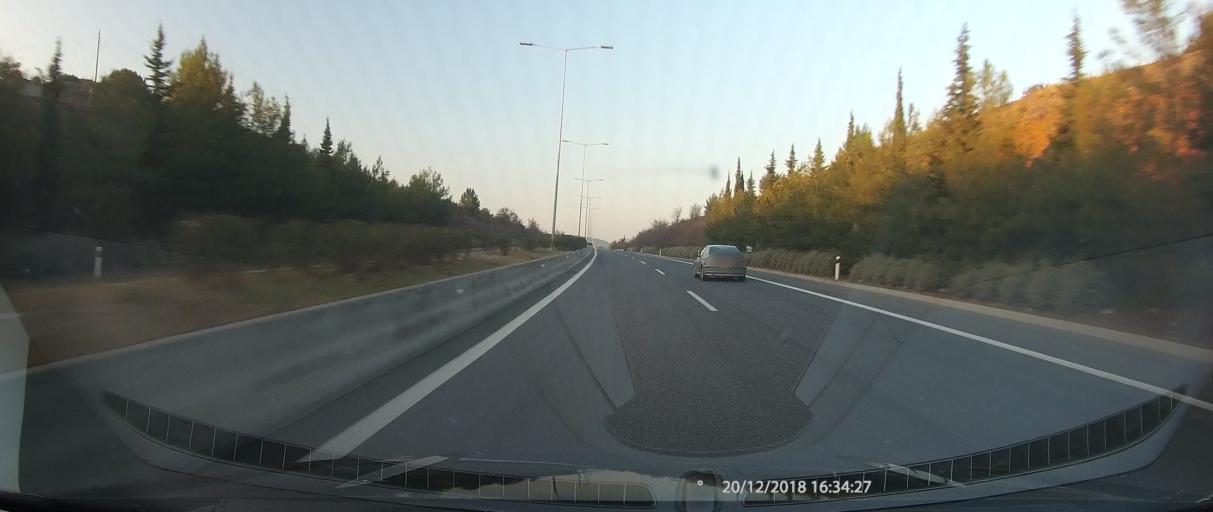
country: GR
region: Thessaly
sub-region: Nomos Magnisias
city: Nea Anchialos
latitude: 39.2827
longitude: 22.7456
